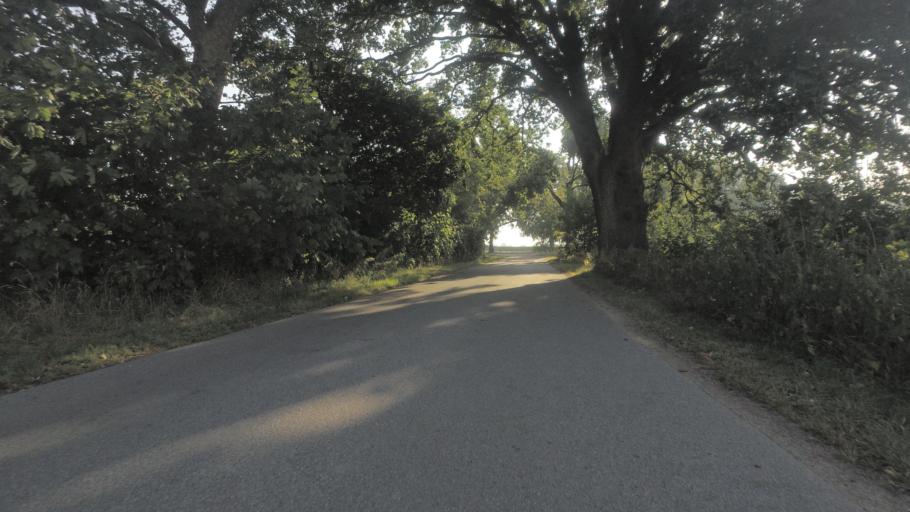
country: DE
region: Mecklenburg-Vorpommern
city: Malchow
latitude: 53.3540
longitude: 12.3631
